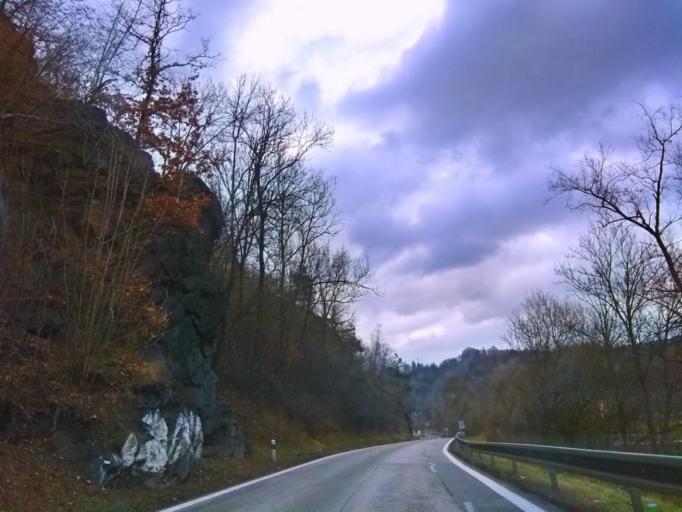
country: CZ
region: Jihocesky
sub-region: Okres Cesky Krumlov
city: Cesky Krumlov
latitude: 48.7976
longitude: 14.3050
